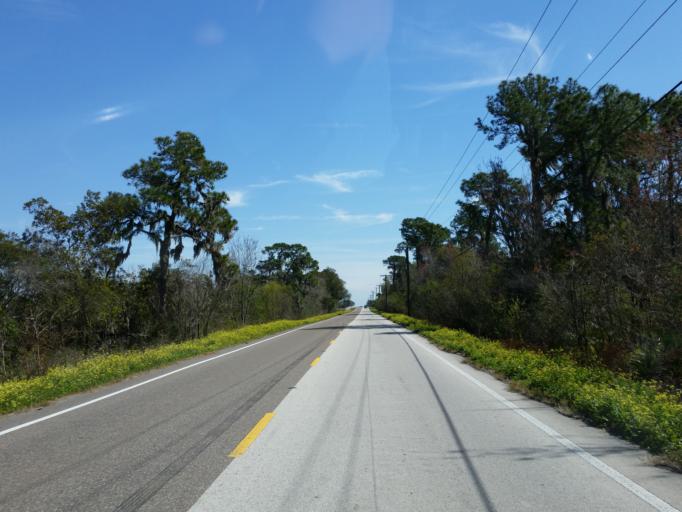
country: US
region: Florida
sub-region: Hillsborough County
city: Balm
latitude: 27.7626
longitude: -82.2106
